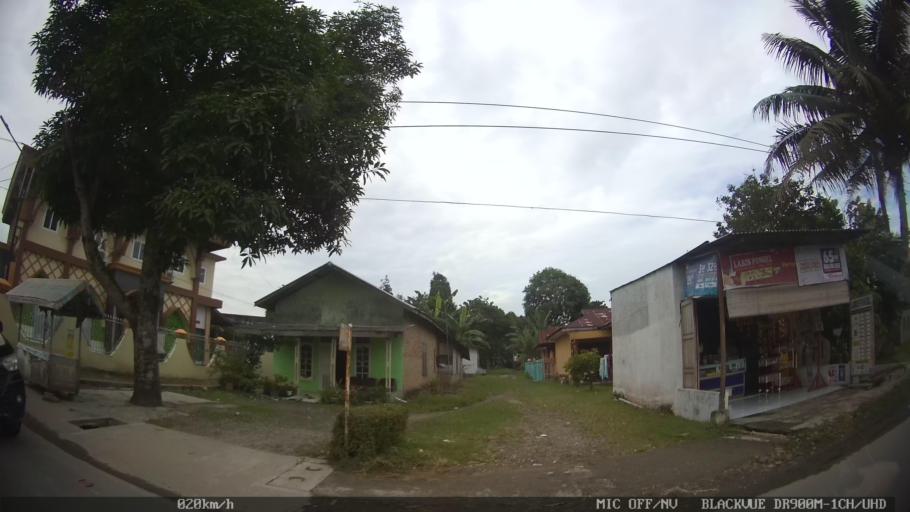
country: ID
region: North Sumatra
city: Sunggal
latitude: 3.6264
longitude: 98.5938
